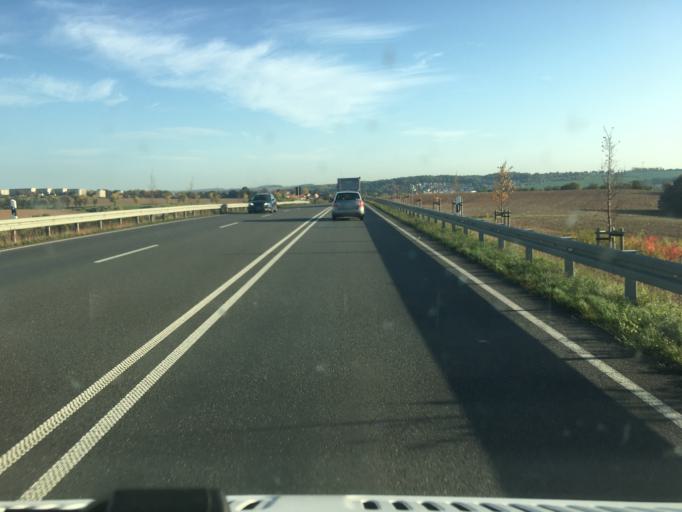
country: DE
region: Saxony
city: Neukirchen
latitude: 50.7958
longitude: 12.3699
